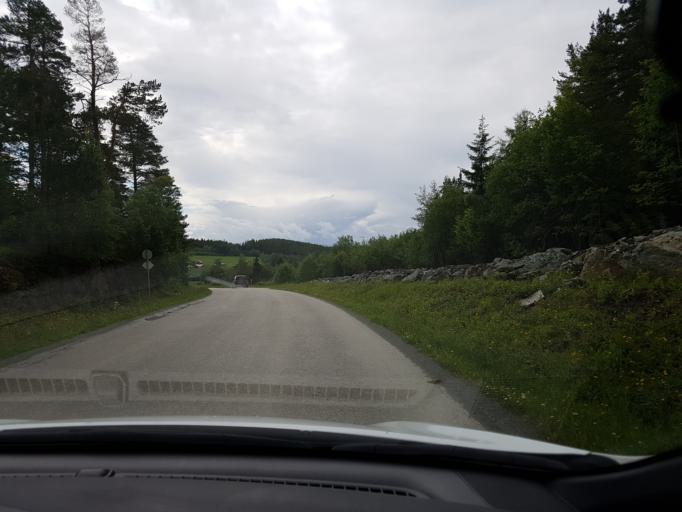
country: NO
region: Nord-Trondelag
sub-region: Frosta
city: Frosta
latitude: 63.6032
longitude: 10.7340
